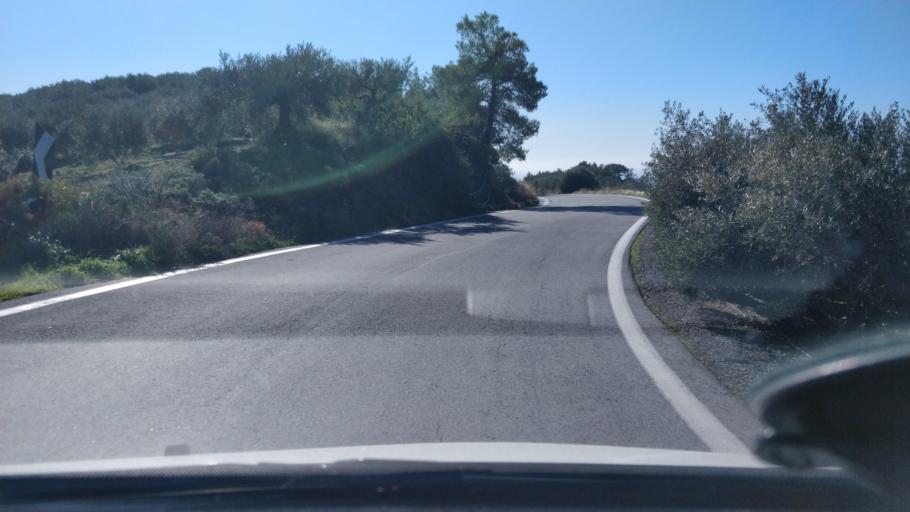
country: GR
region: Crete
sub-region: Nomos Irakleiou
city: Kastelli
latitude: 35.0277
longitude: 25.4494
